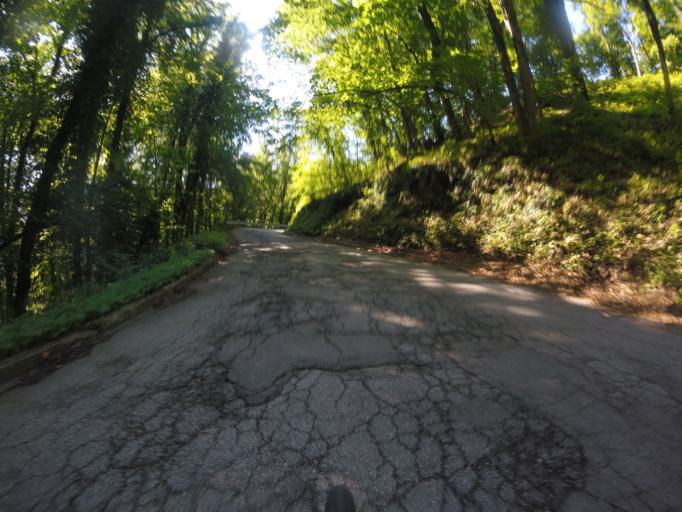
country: SI
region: Brezice
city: Brezice
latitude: 45.8381
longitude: 15.5982
